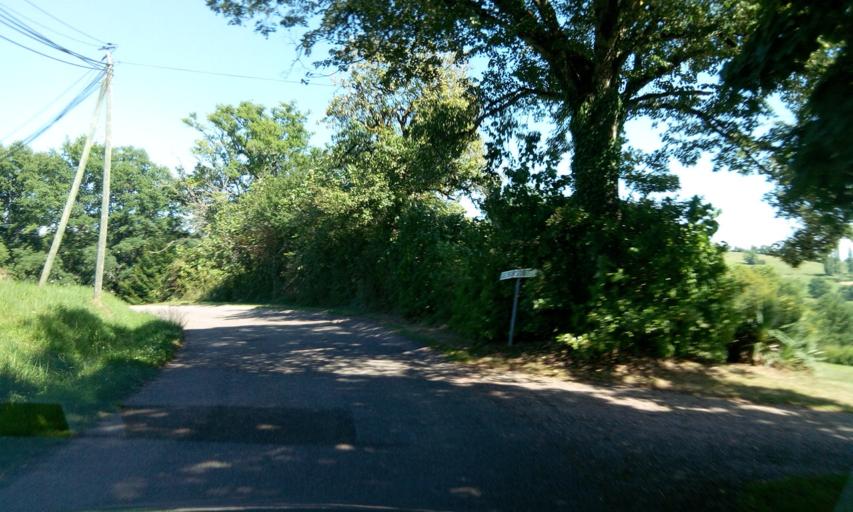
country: FR
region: Limousin
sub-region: Departement de la Correze
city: Beynat
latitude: 45.0548
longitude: 1.7593
